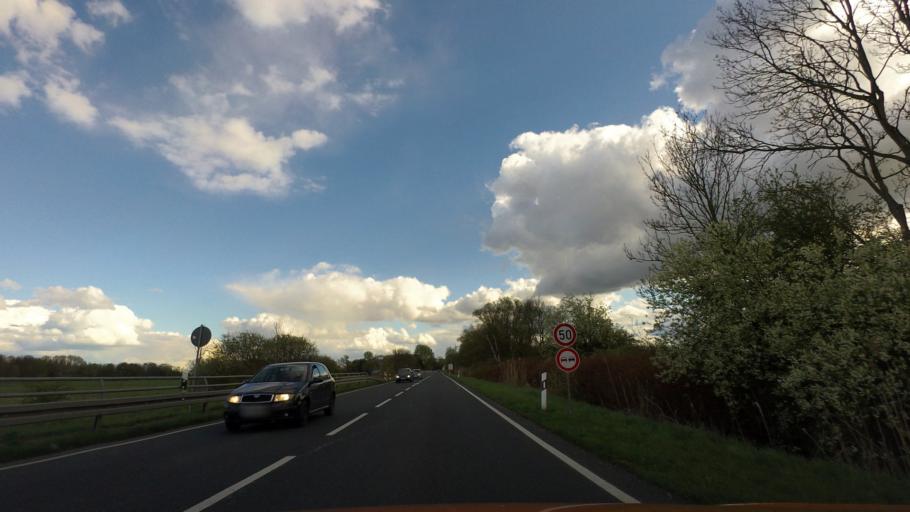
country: DE
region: Brandenburg
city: Friesack
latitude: 52.7774
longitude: 12.5593
